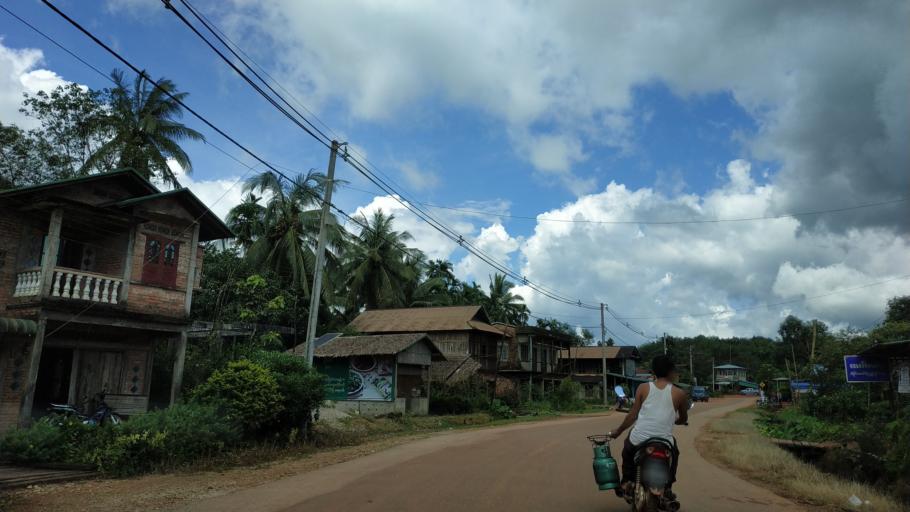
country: MM
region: Tanintharyi
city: Dawei
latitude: 14.2780
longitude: 98.1558
